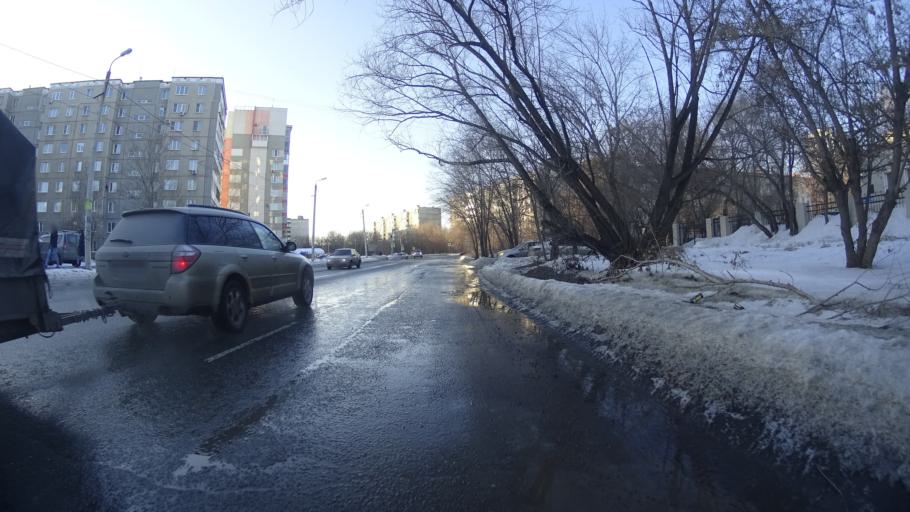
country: RU
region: Chelyabinsk
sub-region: Gorod Chelyabinsk
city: Chelyabinsk
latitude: 55.1370
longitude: 61.4490
